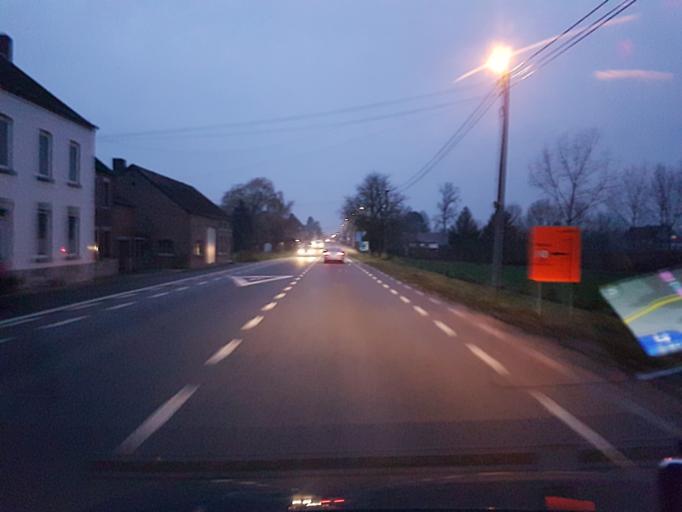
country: BE
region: Wallonia
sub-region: Province du Brabant Wallon
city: Ramillies
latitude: 50.6303
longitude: 4.8697
